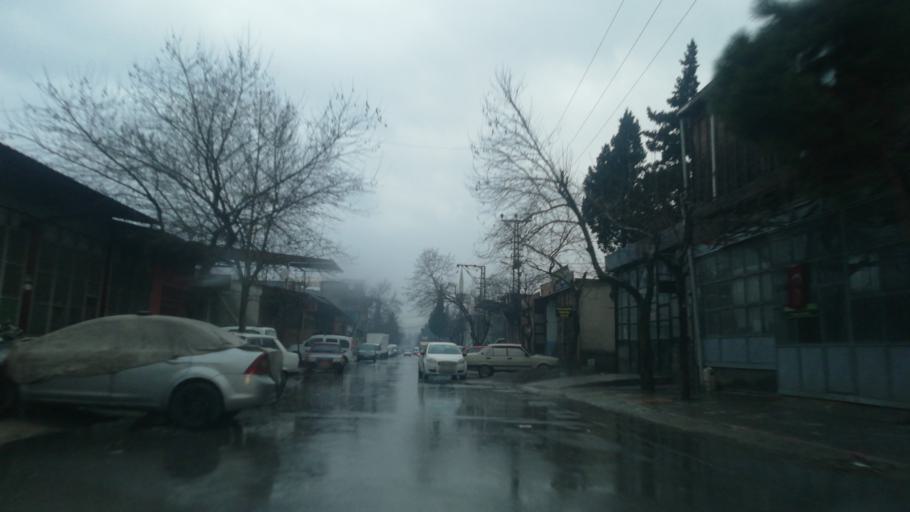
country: TR
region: Kahramanmaras
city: Kahramanmaras
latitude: 37.5607
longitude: 36.9602
